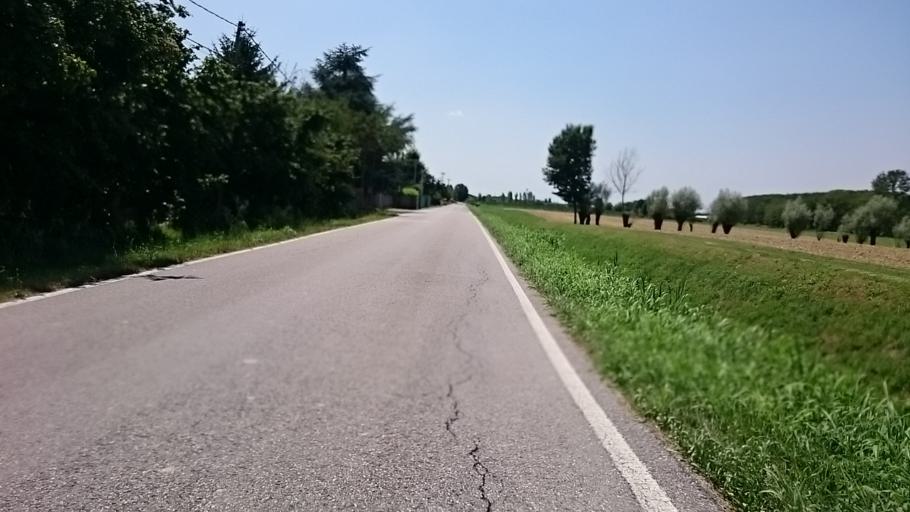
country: IT
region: Veneto
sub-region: Provincia di Venezia
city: Sant'Angelo
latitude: 45.5174
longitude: 11.9971
